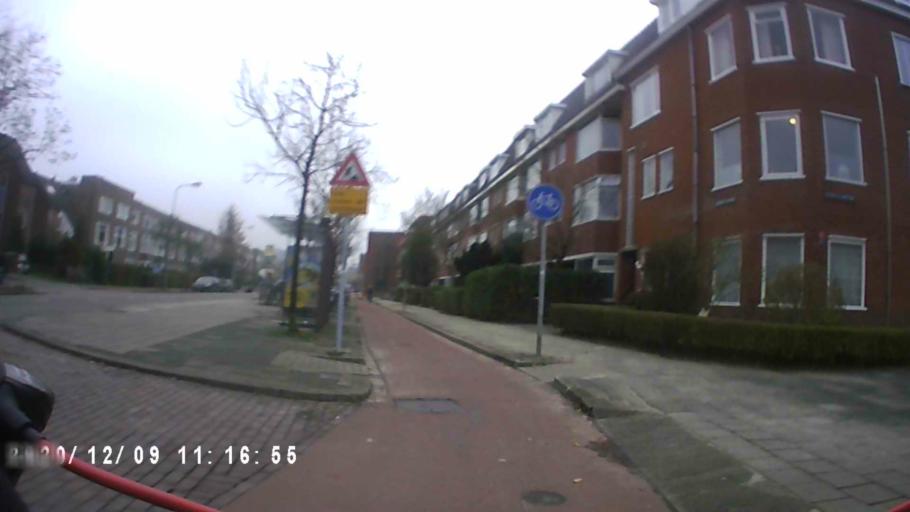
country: NL
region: Groningen
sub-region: Gemeente Groningen
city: Groningen
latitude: 53.2179
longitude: 6.5446
